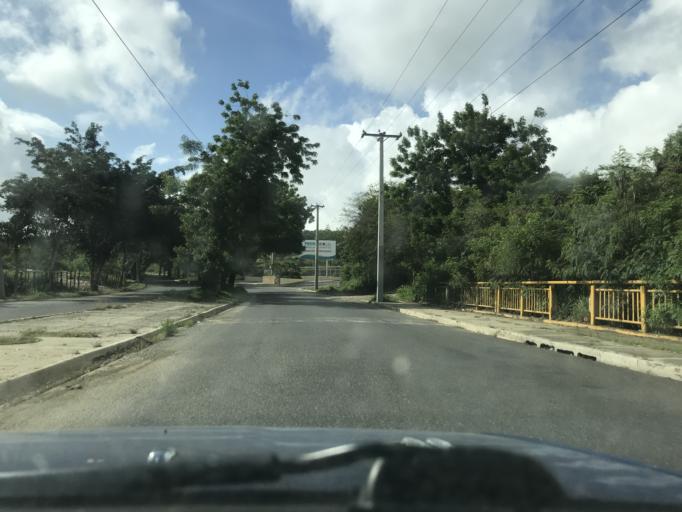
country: DO
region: Santiago
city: Santiago de los Caballeros
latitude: 19.4144
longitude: -70.7293
